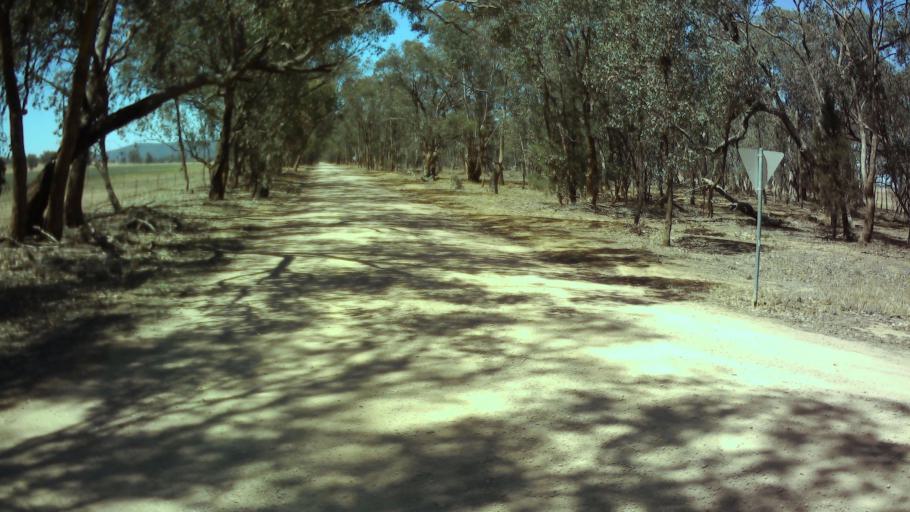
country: AU
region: New South Wales
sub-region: Weddin
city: Grenfell
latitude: -33.9076
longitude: 148.0803
